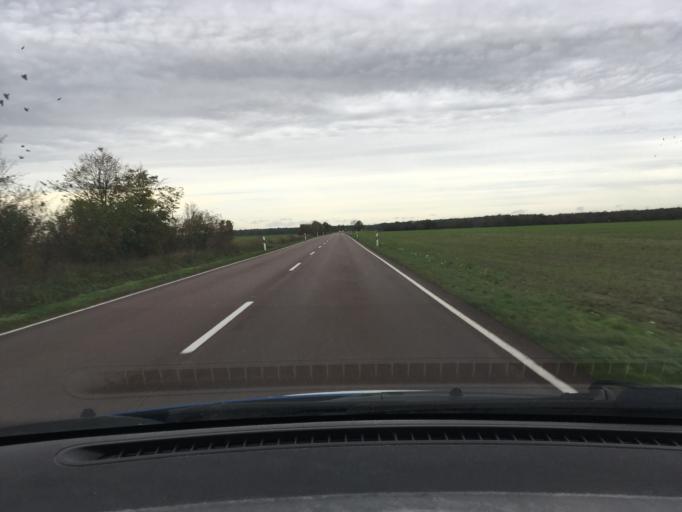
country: DE
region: Saxony-Anhalt
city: Leitzkau
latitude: 52.0219
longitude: 12.0050
